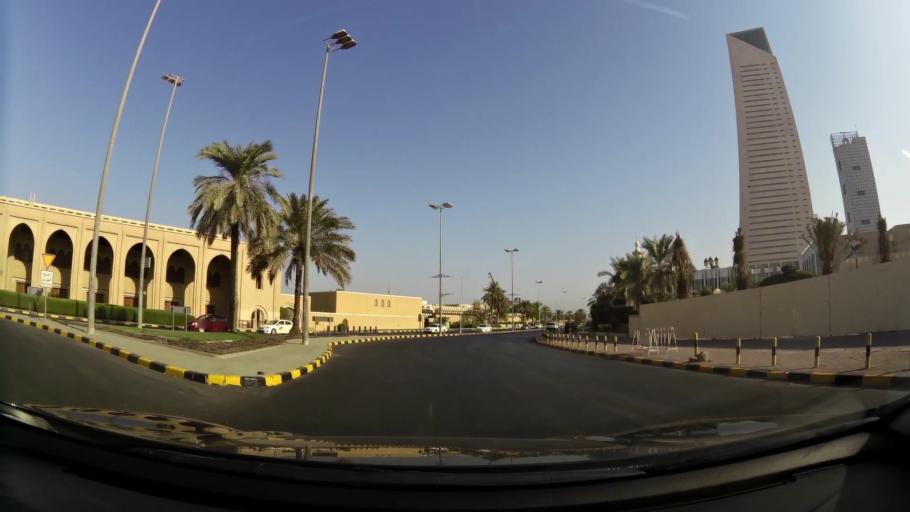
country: KW
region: Al Asimah
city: Kuwait City
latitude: 29.3801
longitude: 47.9739
